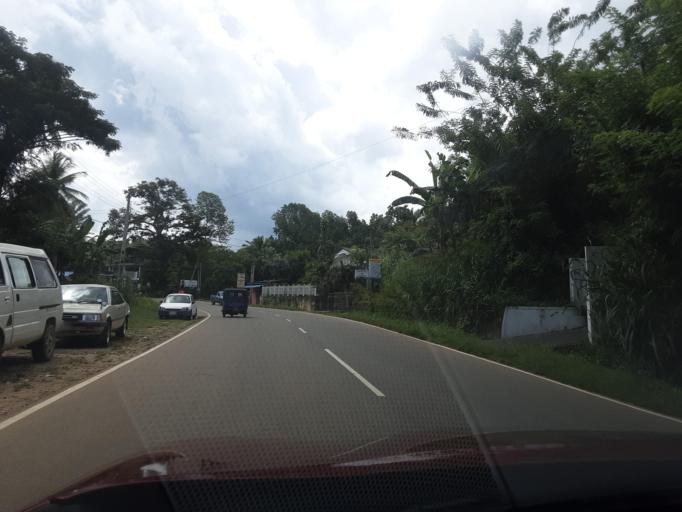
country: LK
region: Uva
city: Monaragala
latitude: 6.8979
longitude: 81.2405
